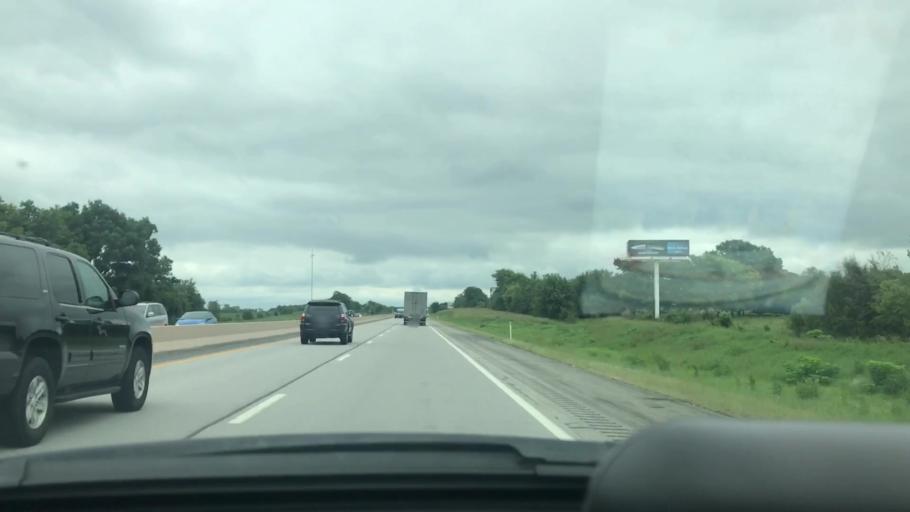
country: US
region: Oklahoma
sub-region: Ottawa County
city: Commerce
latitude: 36.9070
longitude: -94.7958
